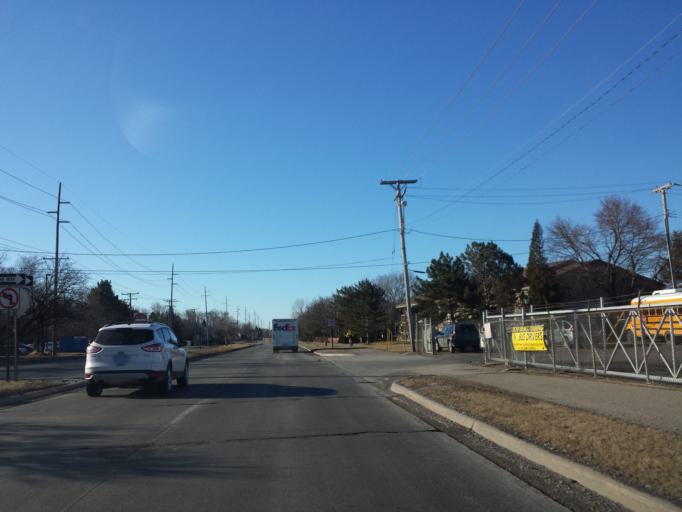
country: US
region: Michigan
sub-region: Oakland County
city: Rochester Hills
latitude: 42.6767
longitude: -83.1535
